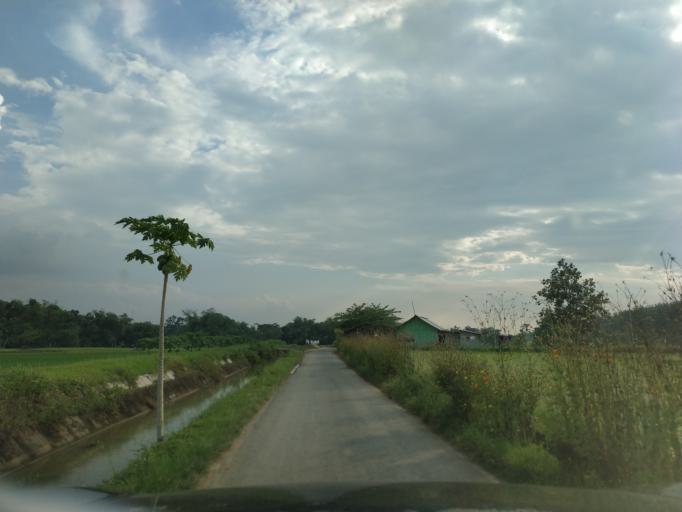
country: ID
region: Central Java
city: Tempuran
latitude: -6.9091
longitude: 111.4616
